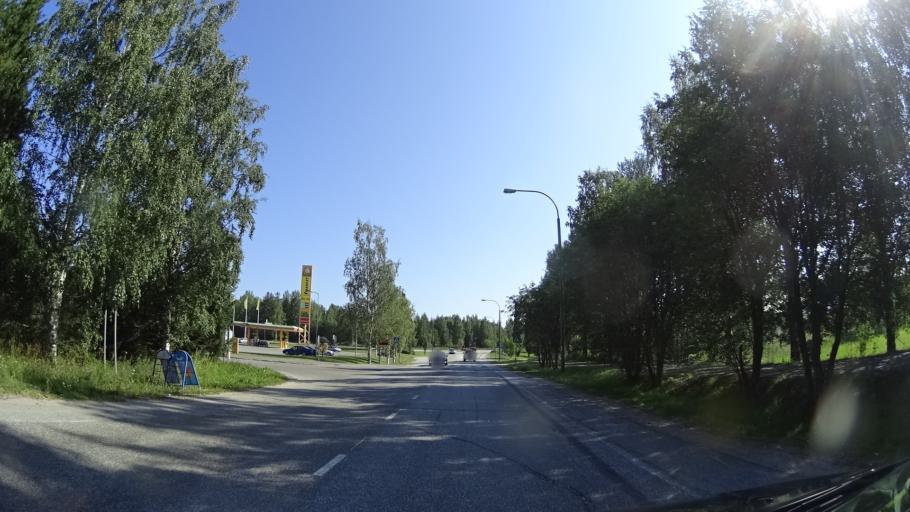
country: FI
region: North Karelia
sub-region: Joensuu
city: Juuka
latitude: 63.2463
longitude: 29.2646
